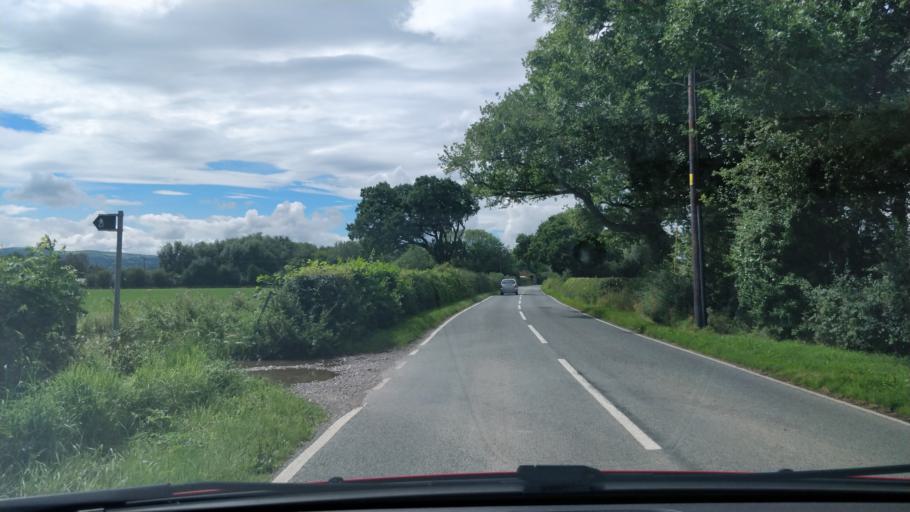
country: GB
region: Wales
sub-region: Wrexham
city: Rossett
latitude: 53.1530
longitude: -2.9736
